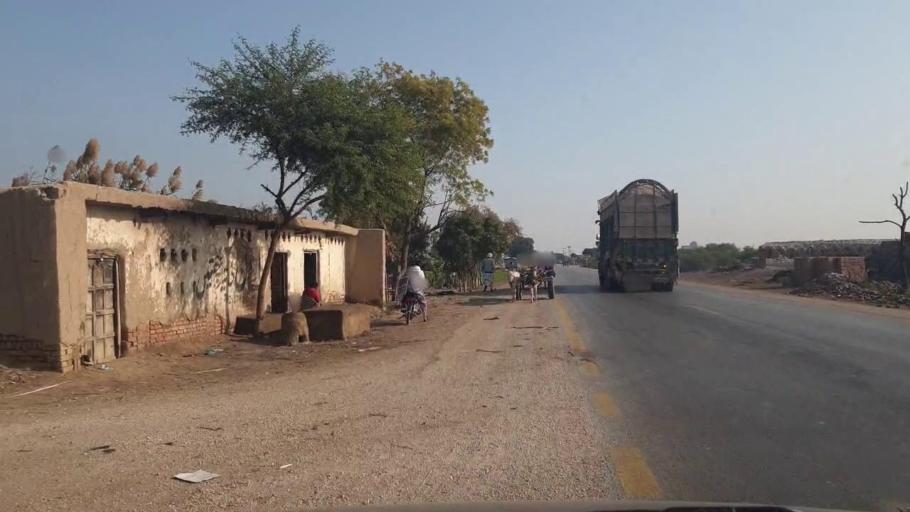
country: PK
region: Sindh
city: Tando Adam
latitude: 25.7360
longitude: 68.6173
